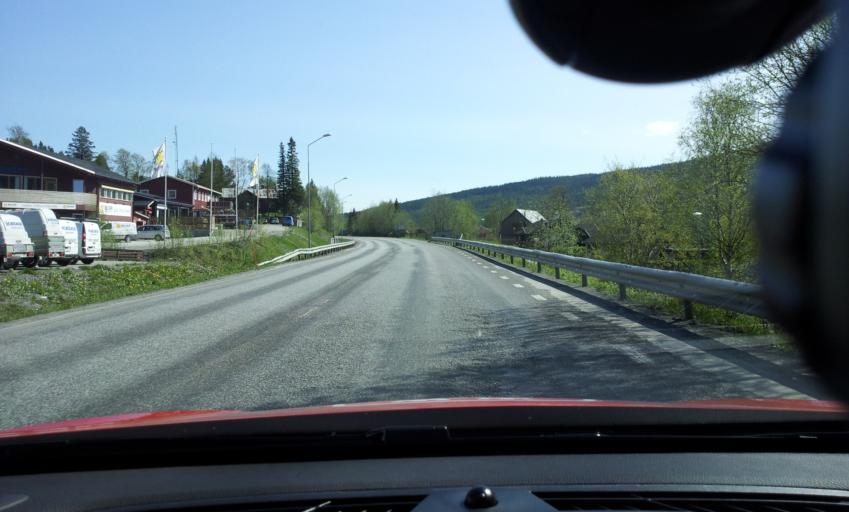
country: SE
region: Jaemtland
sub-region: Are Kommun
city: Are
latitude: 63.3931
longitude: 13.0938
